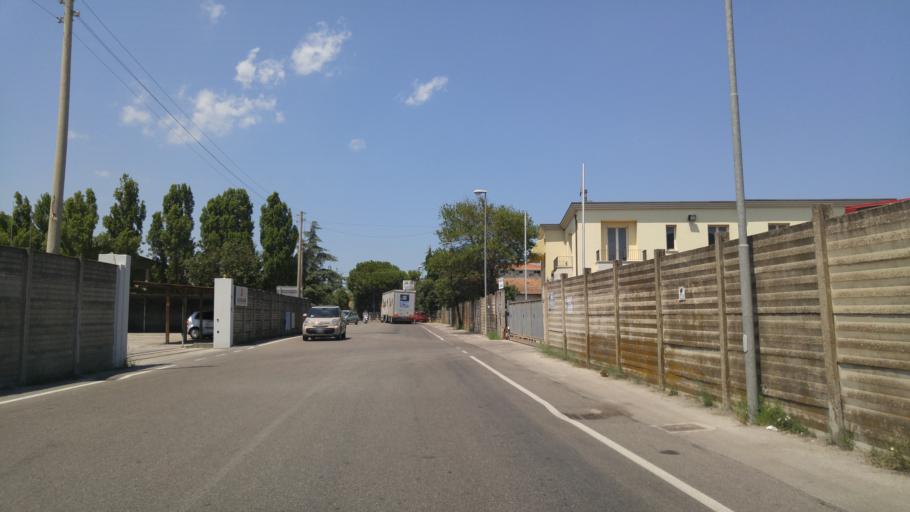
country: IT
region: Emilia-Romagna
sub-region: Provincia di Rimini
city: Montalbano
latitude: 43.9484
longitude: 12.7281
